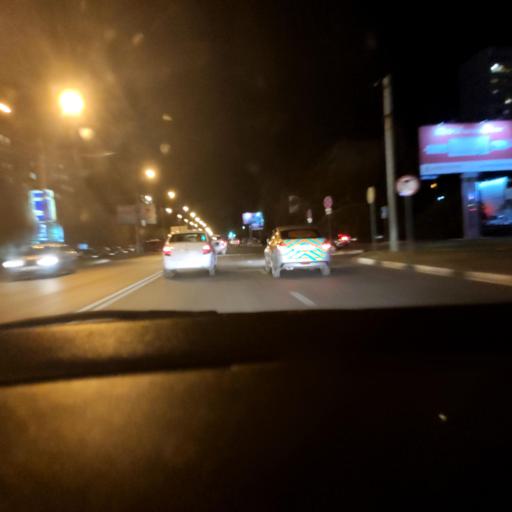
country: RU
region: Voronezj
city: Voronezh
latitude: 51.7067
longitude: 39.1731
